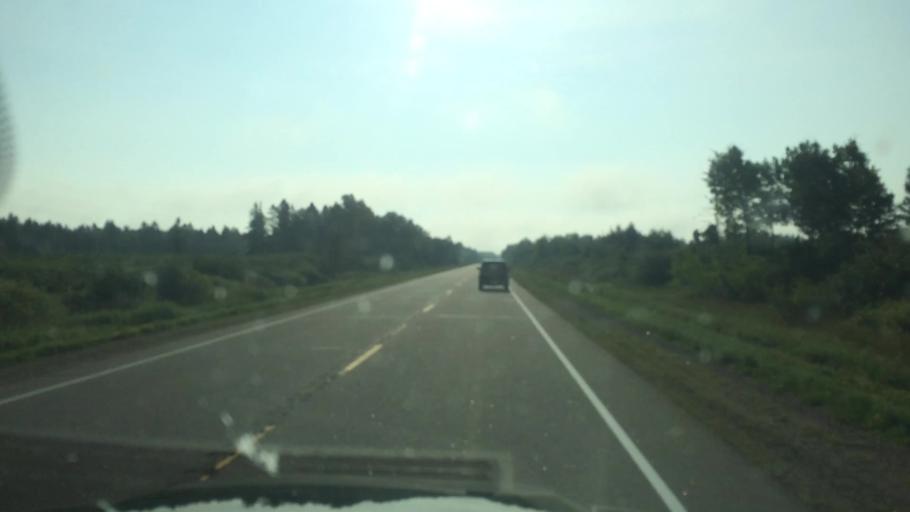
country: US
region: Wisconsin
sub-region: Langlade County
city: Antigo
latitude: 45.1464
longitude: -89.3358
